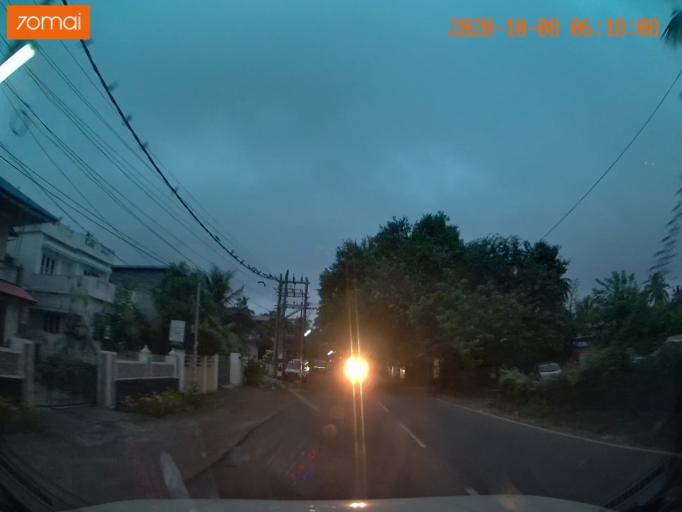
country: IN
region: Kerala
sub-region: Thrissur District
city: Trichur
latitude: 10.5121
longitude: 76.2505
